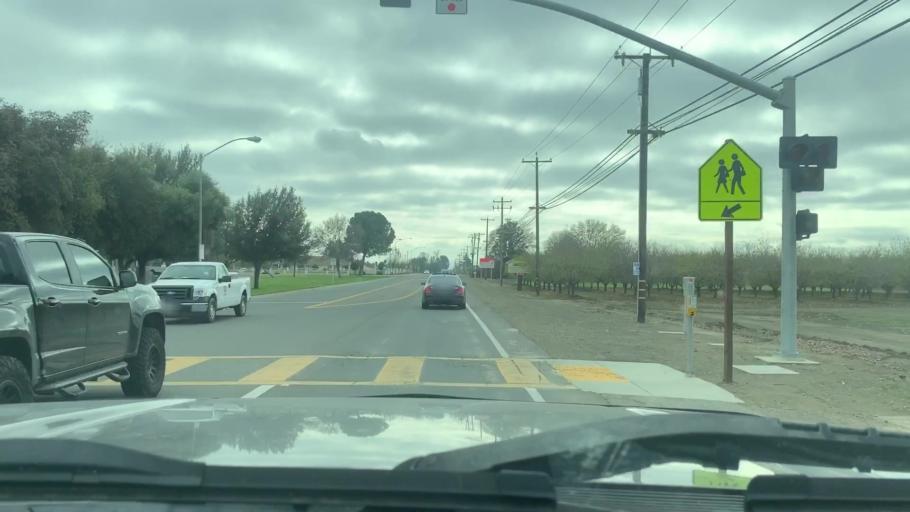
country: US
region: California
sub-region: Merced County
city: Los Banos
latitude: 37.0495
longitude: -120.8356
